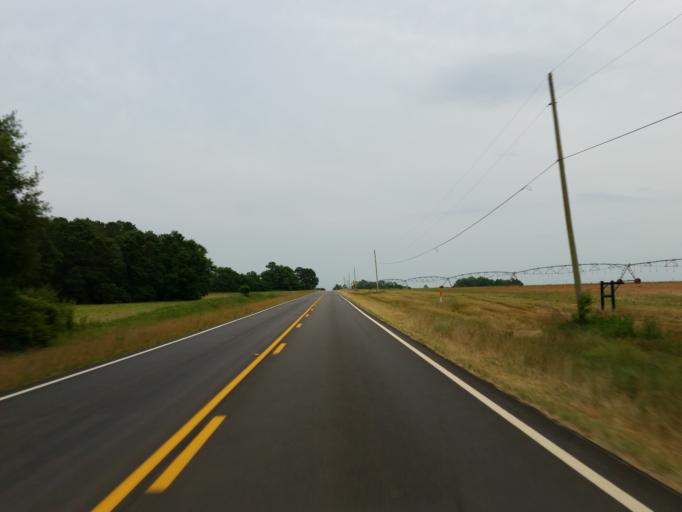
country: US
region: Georgia
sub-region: Dooly County
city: Unadilla
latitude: 32.3158
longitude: -83.7734
